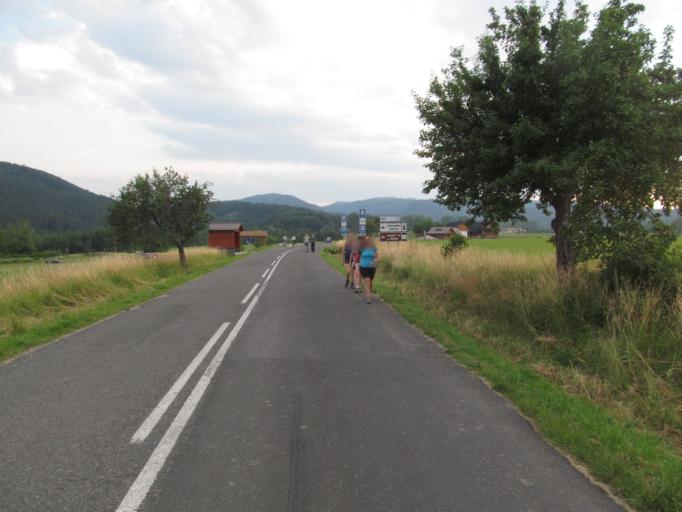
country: SK
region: Presovsky
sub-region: Okres Poprad
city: Poprad
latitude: 48.9682
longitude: 20.3886
